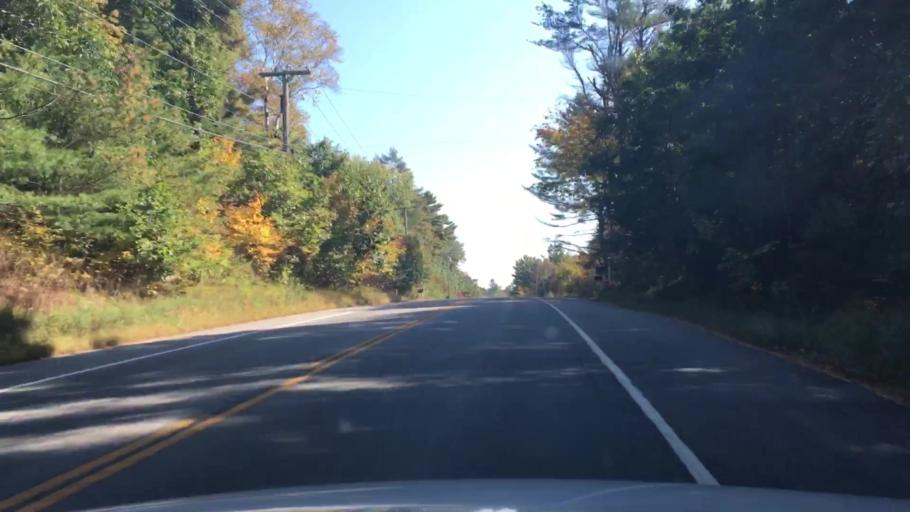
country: US
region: Maine
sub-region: Androscoggin County
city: Lisbon Falls
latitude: 43.9804
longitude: -70.0312
